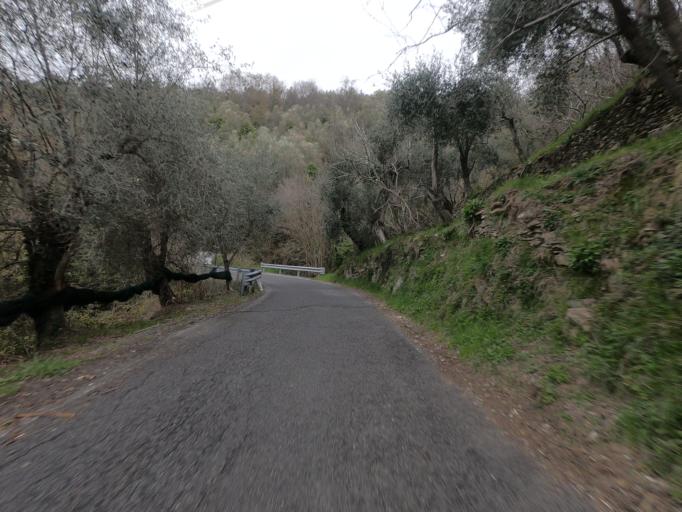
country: IT
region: Liguria
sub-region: Provincia di Savona
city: Testico
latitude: 44.0255
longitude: 8.0047
